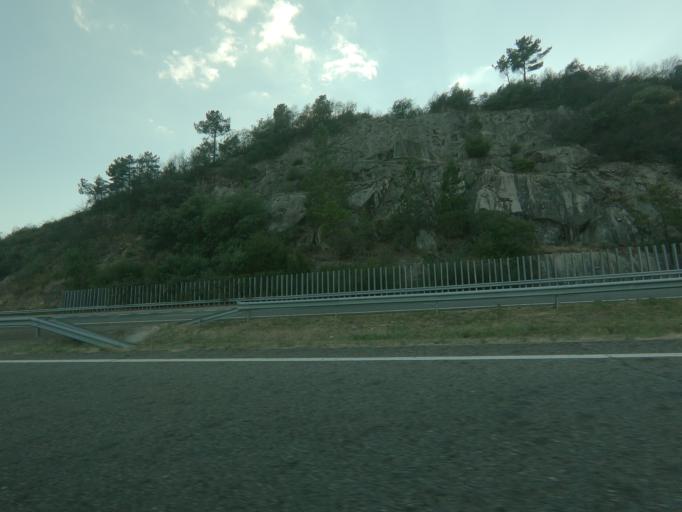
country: ES
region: Galicia
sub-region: Provincia de Ourense
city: Oimbra
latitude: 41.9319
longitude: -7.5006
